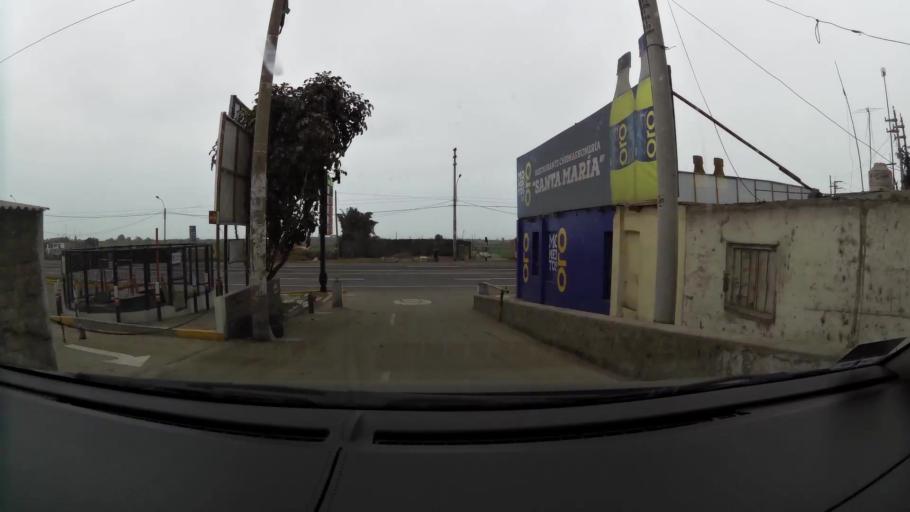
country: PE
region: Lima
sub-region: Provincia de Huaral
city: Chancay
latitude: -11.6002
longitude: -77.2480
